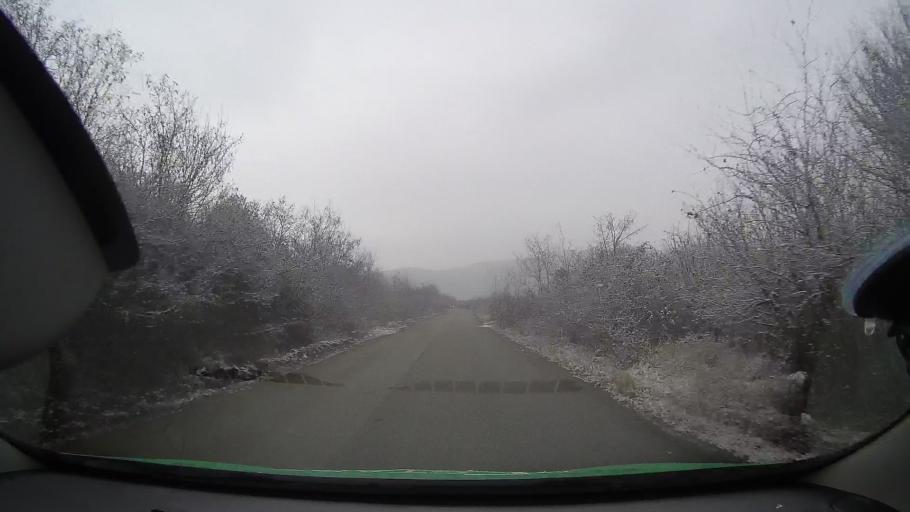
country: RO
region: Alba
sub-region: Comuna Hoparta
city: Hoparta
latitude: 46.3391
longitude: 23.9216
